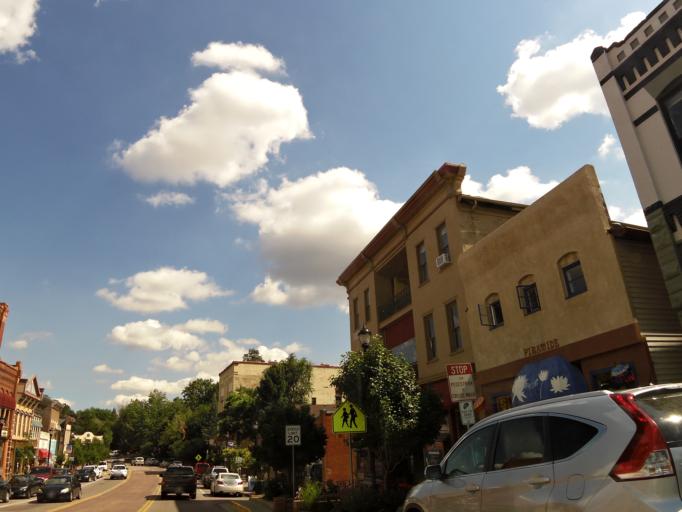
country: US
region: Colorado
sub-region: El Paso County
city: Manitou Springs
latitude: 38.8575
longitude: -104.9162
